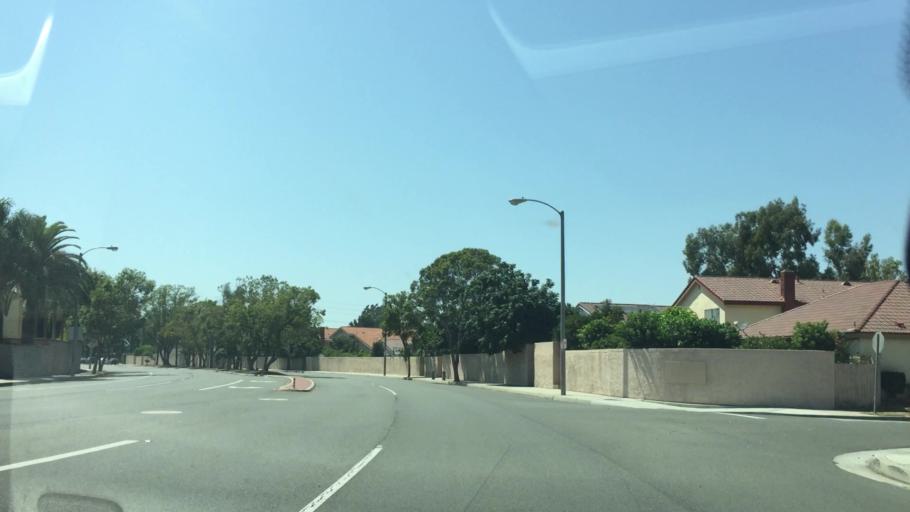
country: US
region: California
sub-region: Orange County
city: Santa Ana
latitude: 33.7085
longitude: -117.9015
